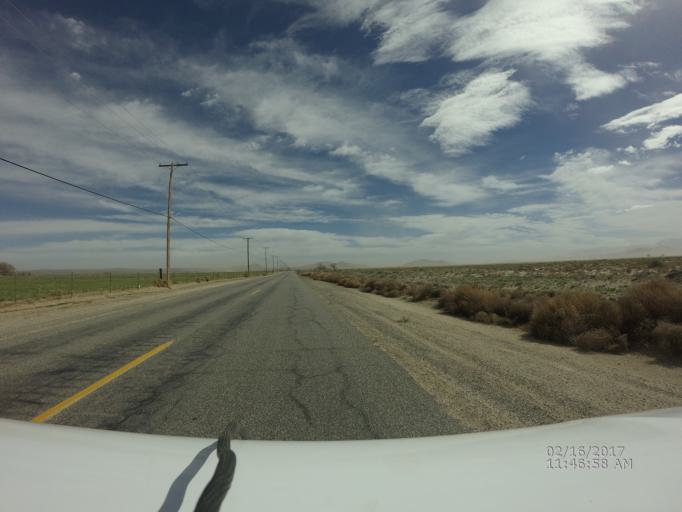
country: US
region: California
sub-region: Los Angeles County
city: Lake Los Angeles
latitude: 34.6900
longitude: -117.9296
